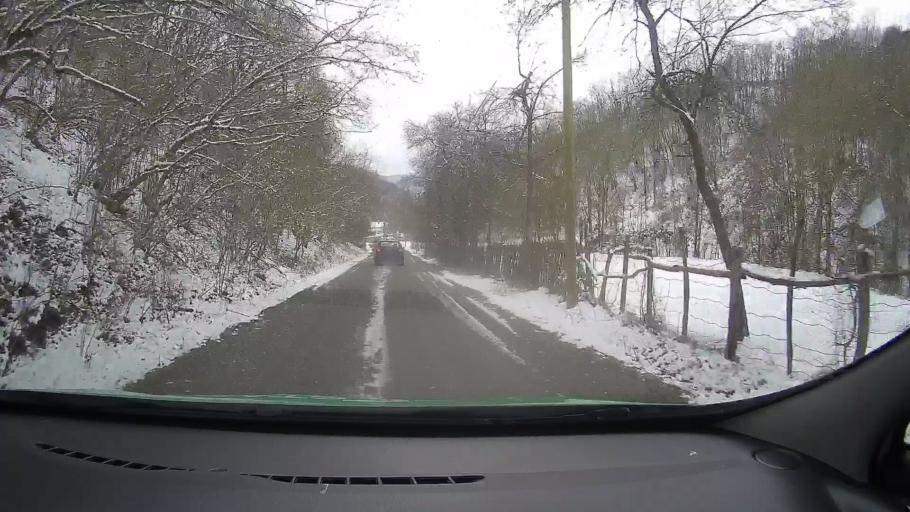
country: RO
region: Alba
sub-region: Comuna Almasu Mare
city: Almasu Mare
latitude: 46.0737
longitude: 23.1085
